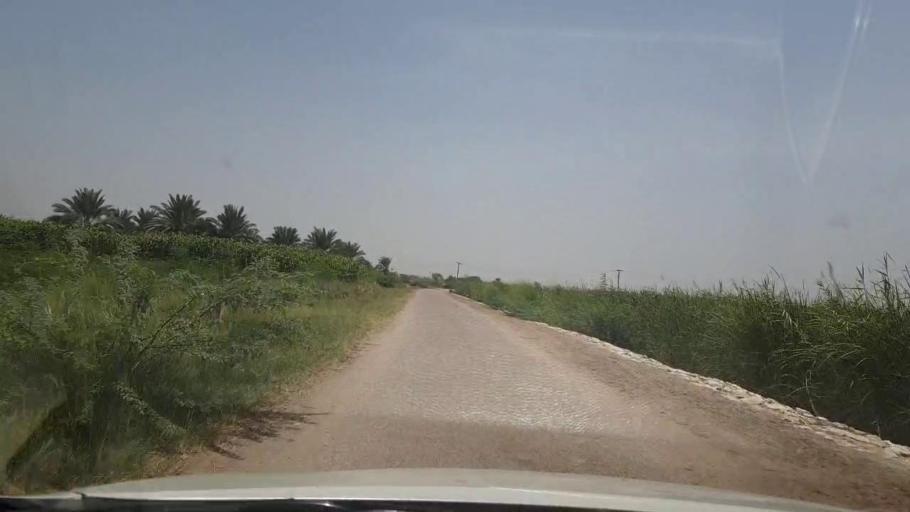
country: PK
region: Sindh
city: Bozdar
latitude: 27.2129
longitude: 68.6623
